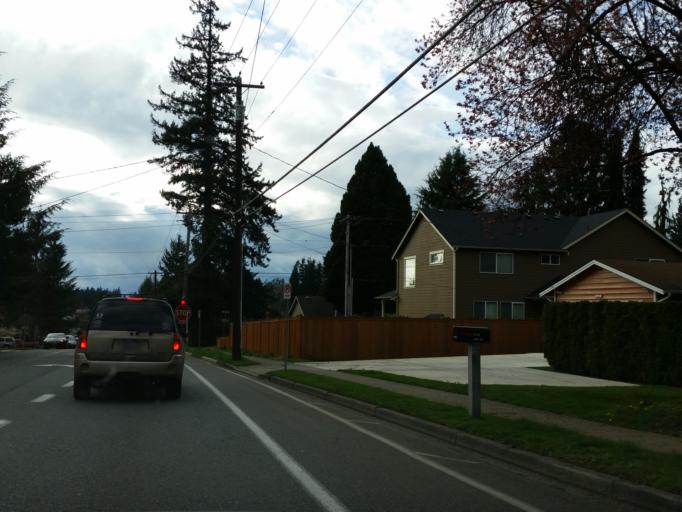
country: US
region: Washington
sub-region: Snohomish County
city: Alderwood Manor
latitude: 47.8283
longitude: -122.2970
